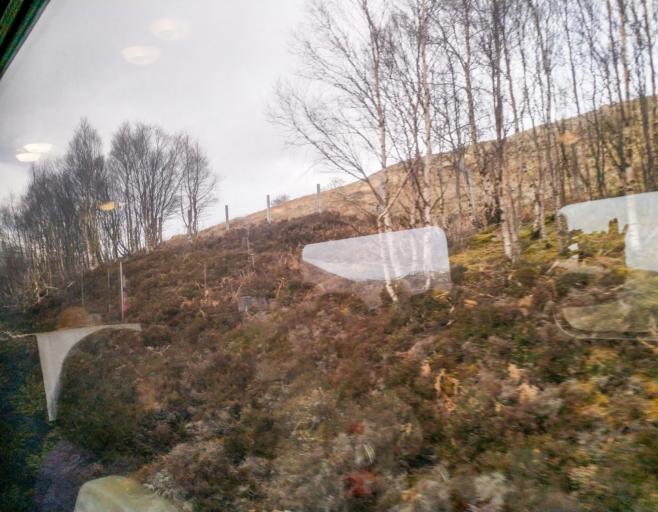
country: GB
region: Scotland
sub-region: Highland
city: Spean Bridge
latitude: 56.7792
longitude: -4.7327
